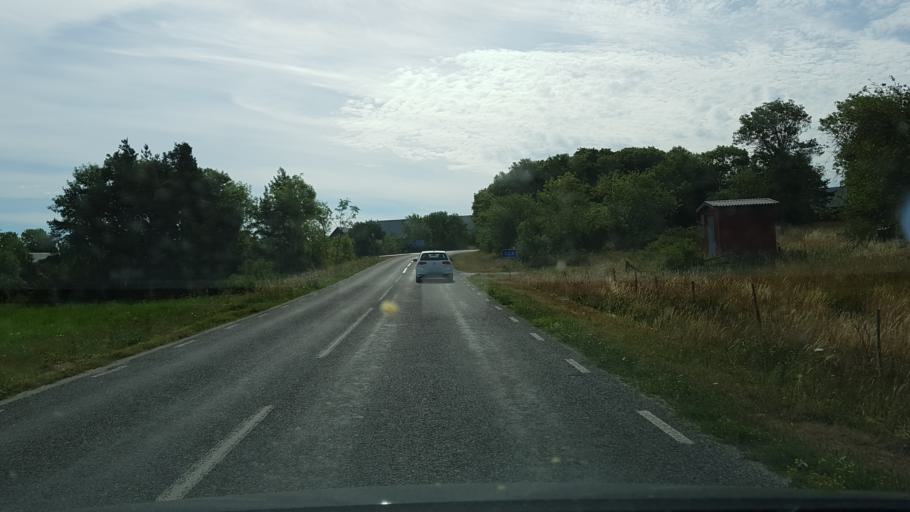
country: SE
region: Gotland
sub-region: Gotland
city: Hemse
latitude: 57.4296
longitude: 18.6284
